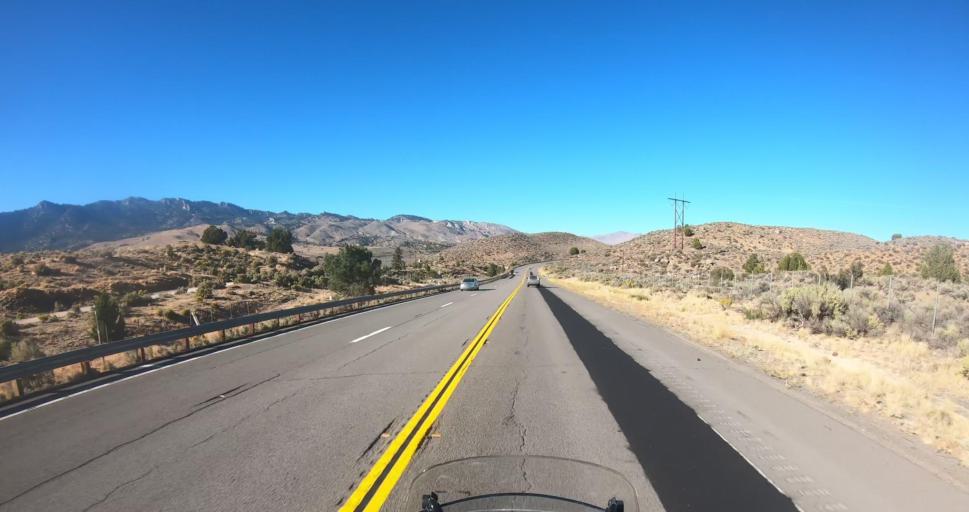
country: US
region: Nevada
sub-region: Washoe County
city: Cold Springs
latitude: 39.8592
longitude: -120.0408
